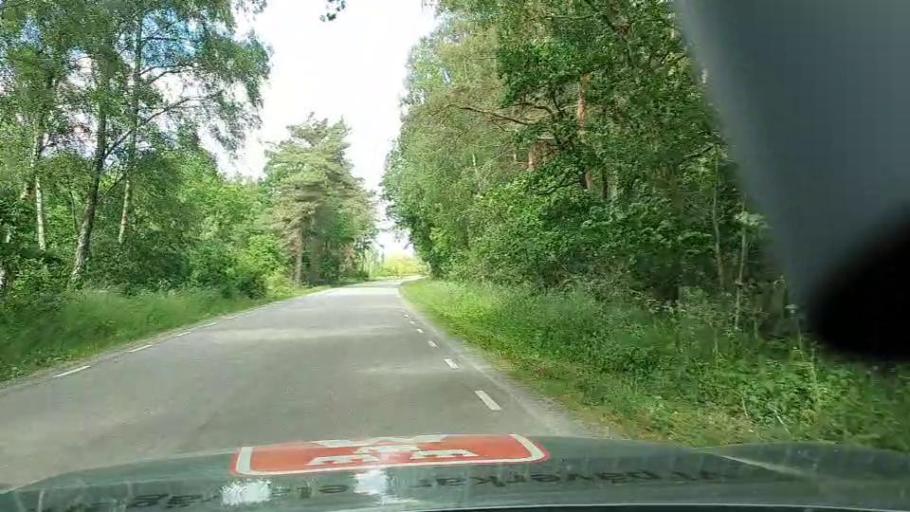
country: SE
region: Blekinge
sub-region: Karlshamns Kommun
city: Morrum
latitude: 56.1023
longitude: 14.6856
